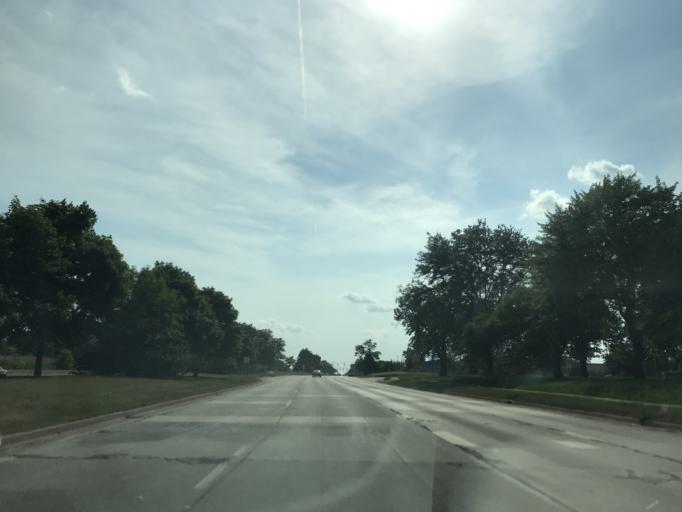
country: US
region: Michigan
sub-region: Wayne County
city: Inkster
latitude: 42.2866
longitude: -83.3421
